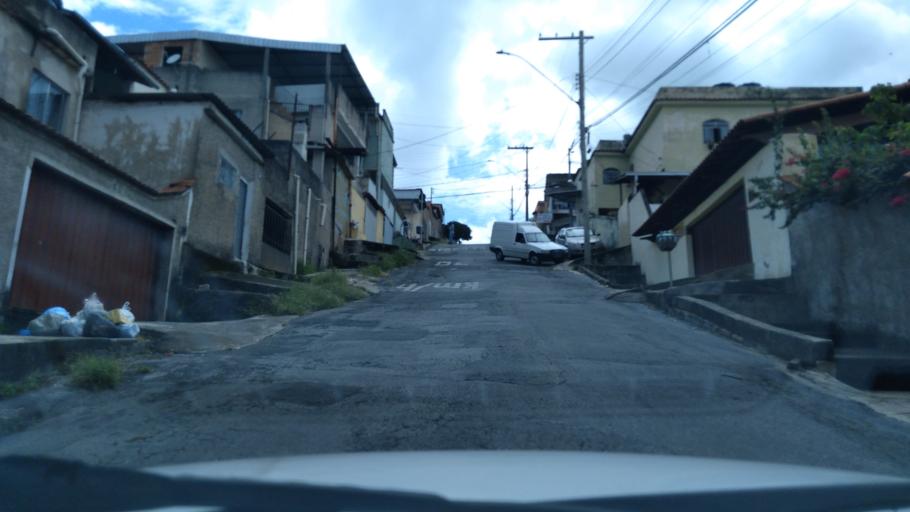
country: BR
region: Minas Gerais
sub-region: Belo Horizonte
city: Belo Horizonte
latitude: -19.8936
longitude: -43.8937
